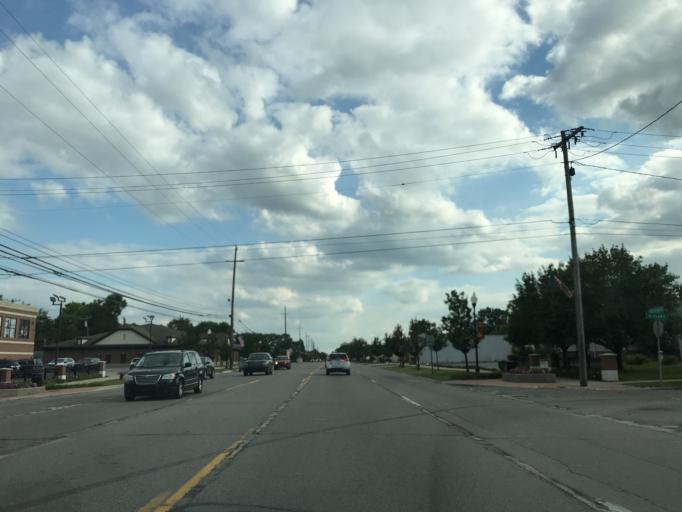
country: US
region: Michigan
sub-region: Wayne County
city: Redford
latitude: 42.4042
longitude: -83.2961
